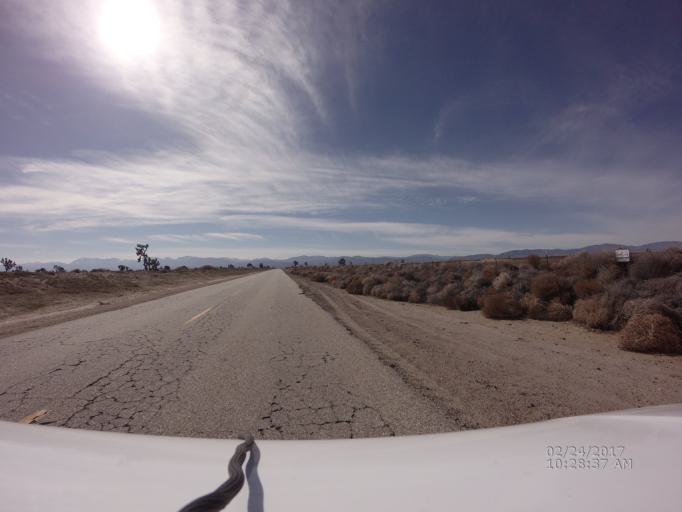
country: US
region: California
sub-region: Los Angeles County
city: Littlerock
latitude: 34.6449
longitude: -118.0053
